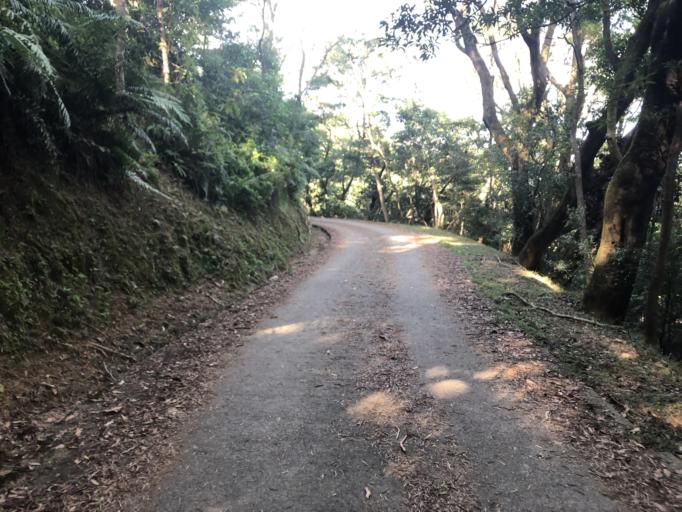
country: HK
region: Tsuen Wan
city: Tsuen Wan
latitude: 22.3923
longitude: 114.0855
